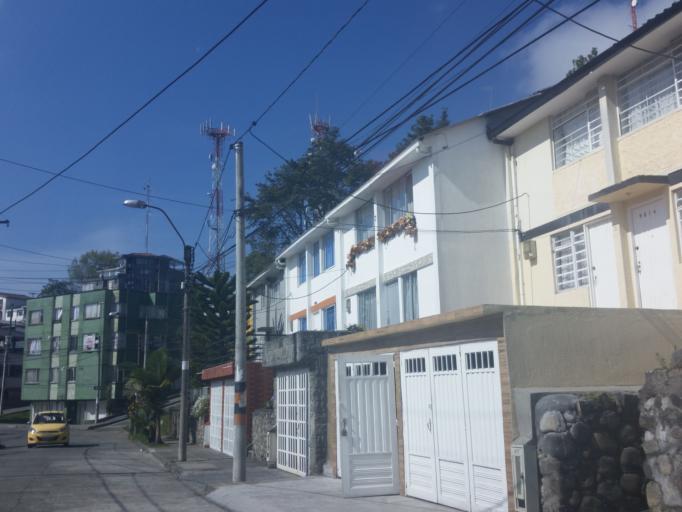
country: CO
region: Caldas
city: Manizales
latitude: 5.0765
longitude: -75.5271
